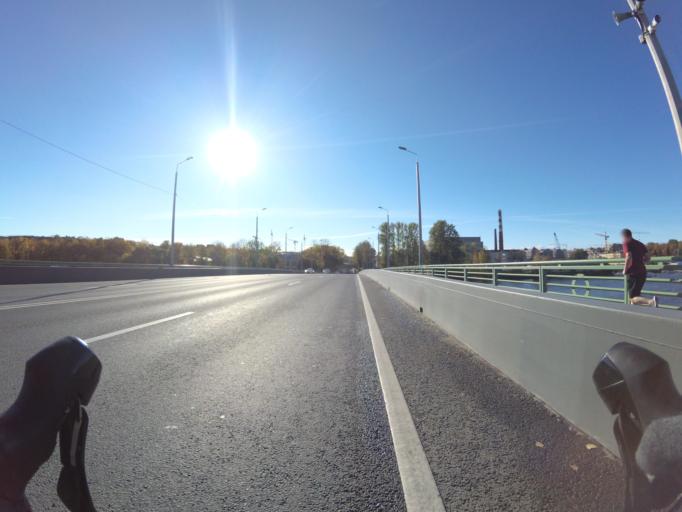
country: RU
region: Leningrad
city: Krestovskiy ostrov
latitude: 59.9651
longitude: 30.2549
